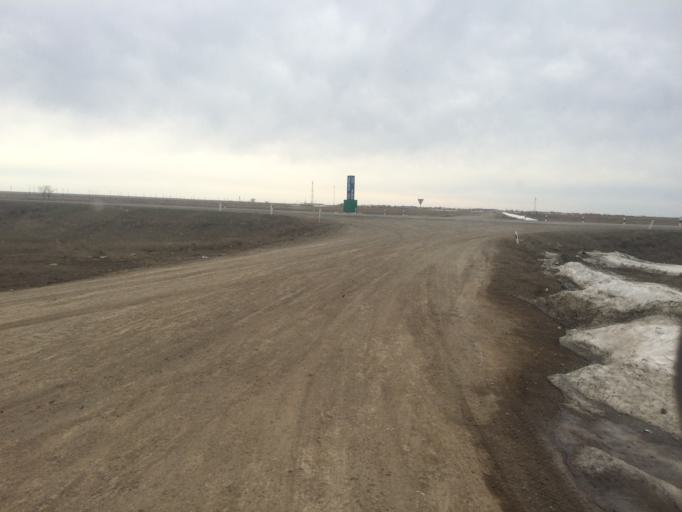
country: KZ
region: Batys Qazaqstan
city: Fedorovka
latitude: 50.6503
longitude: 52.0877
